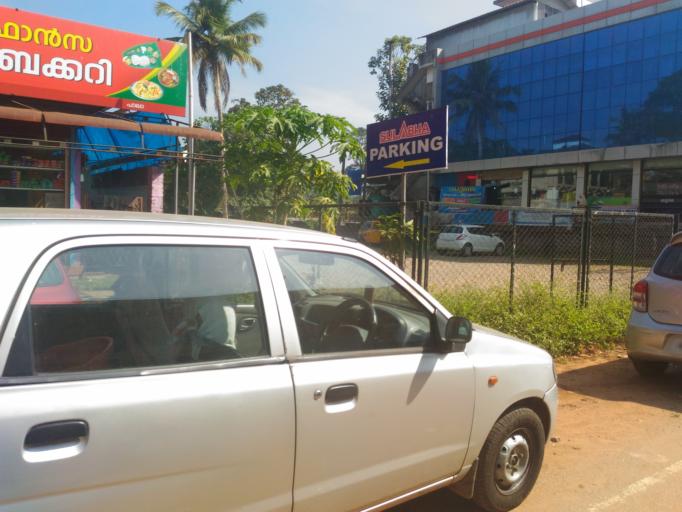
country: IN
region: Kerala
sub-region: Kottayam
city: Lalam
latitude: 9.7141
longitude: 76.6861
